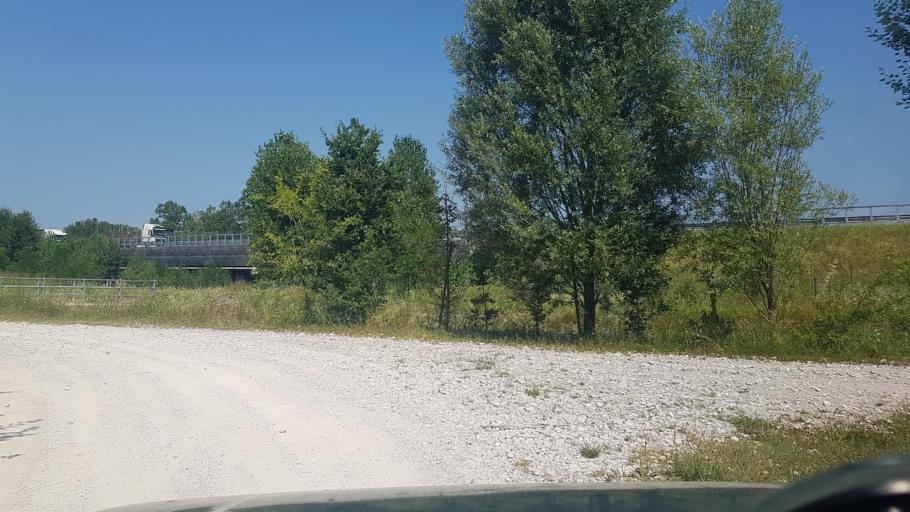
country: IT
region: Friuli Venezia Giulia
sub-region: Provincia di Gorizia
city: Savogna d'Isonzo
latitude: 45.9030
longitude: 13.5602
